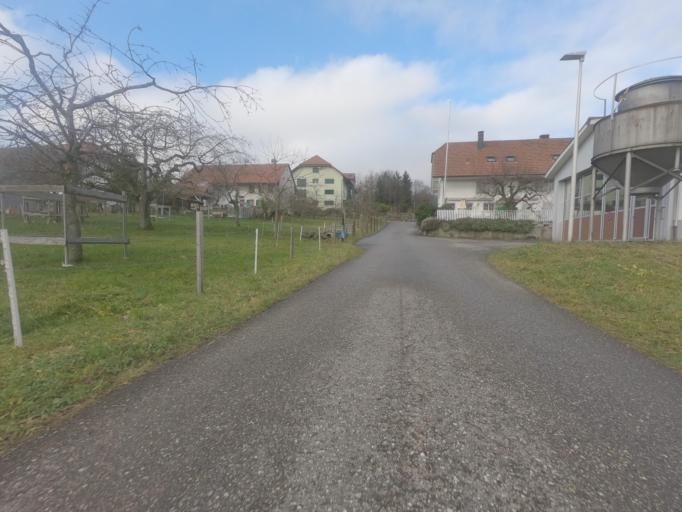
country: CH
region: Solothurn
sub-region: Bezirk Lebern
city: Selzach
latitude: 47.2111
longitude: 7.4846
